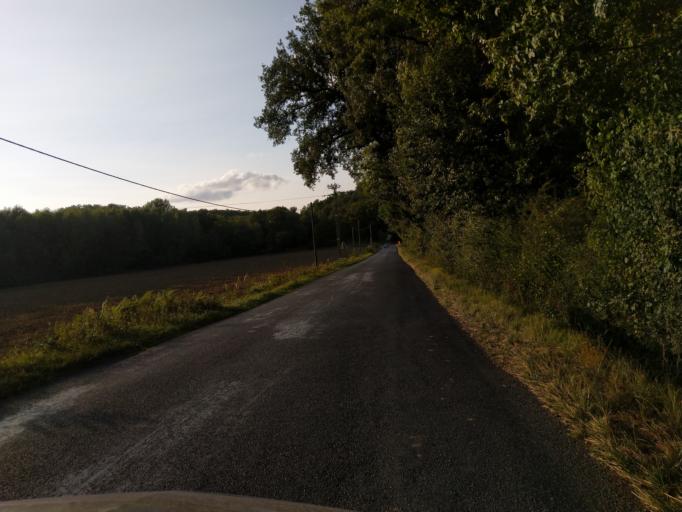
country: FR
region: Midi-Pyrenees
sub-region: Departement du Tarn
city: Frejairolles
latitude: 43.8543
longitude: 2.2384
